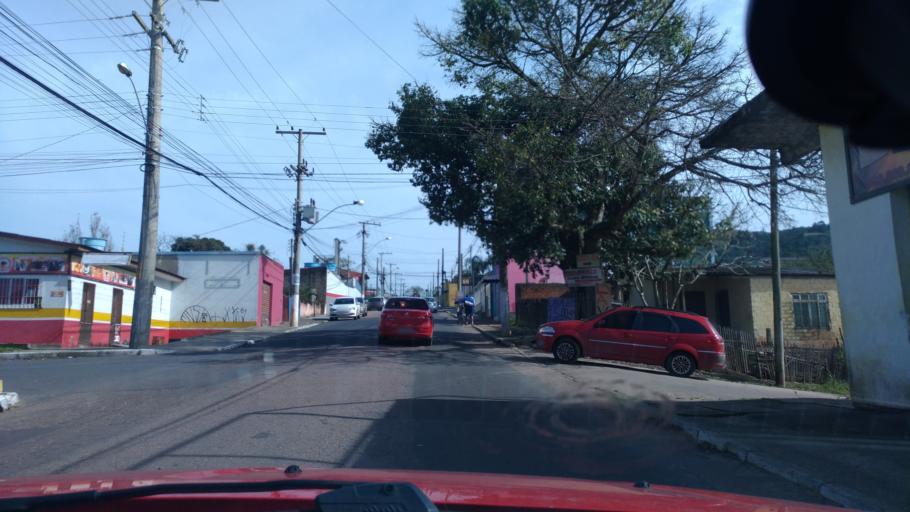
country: BR
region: Rio Grande do Sul
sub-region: Viamao
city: Viamao
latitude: -30.0615
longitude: -51.1056
